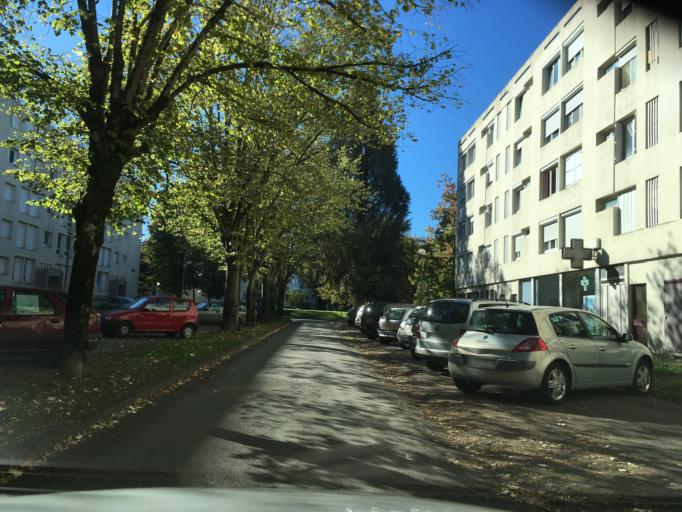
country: FR
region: Aquitaine
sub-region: Departement des Pyrenees-Atlantiques
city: Pau
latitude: 43.3080
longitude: -0.3635
